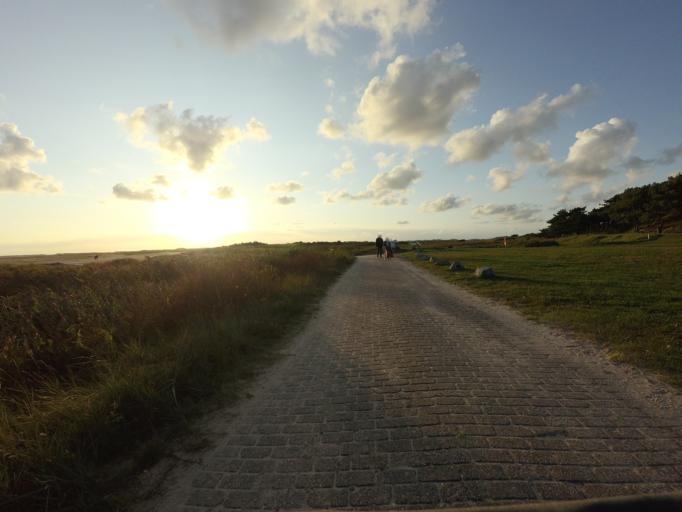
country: NL
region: Friesland
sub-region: Gemeente Terschelling
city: West-Terschelling
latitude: 53.3573
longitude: 5.2096
